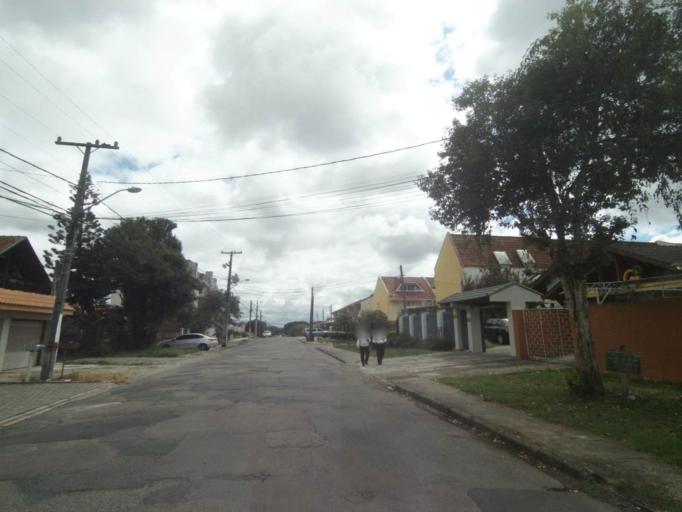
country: BR
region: Parana
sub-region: Curitiba
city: Curitiba
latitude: -25.4863
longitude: -49.2764
